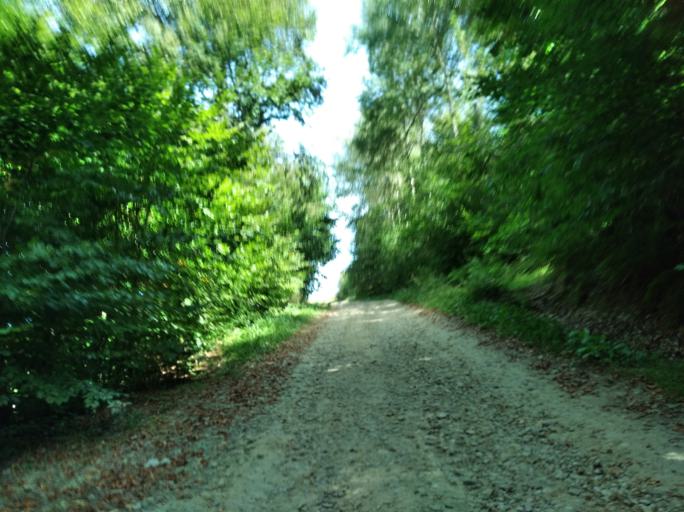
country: PL
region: Subcarpathian Voivodeship
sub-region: Powiat ropczycko-sedziszowski
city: Wielopole Skrzynskie
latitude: 49.9157
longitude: 21.6290
